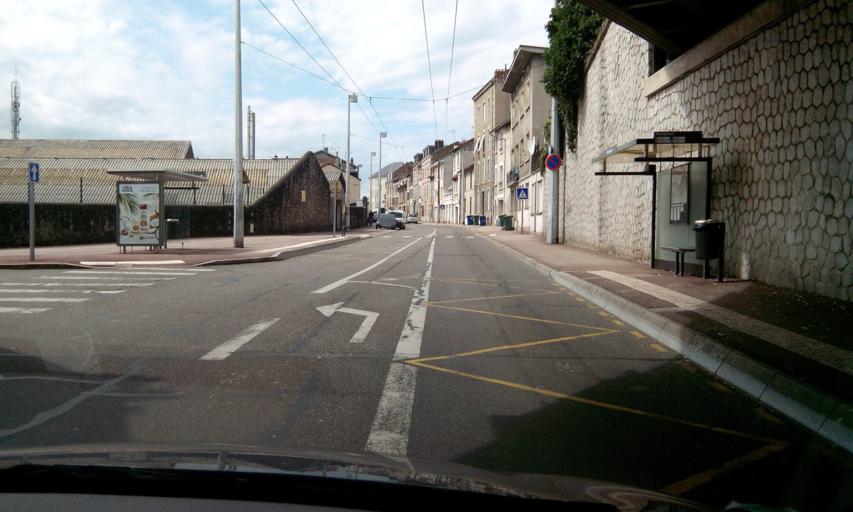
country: FR
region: Limousin
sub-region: Departement de la Haute-Vienne
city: Limoges
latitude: 45.8414
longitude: 1.2710
